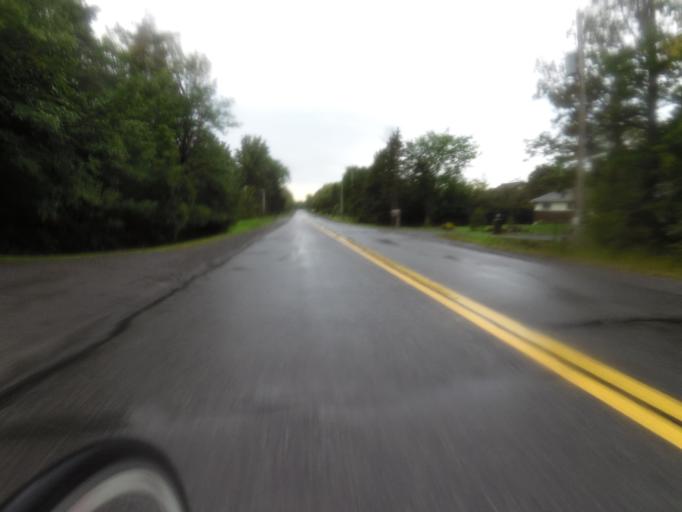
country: CA
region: Ontario
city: Bells Corners
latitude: 45.1966
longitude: -75.7162
